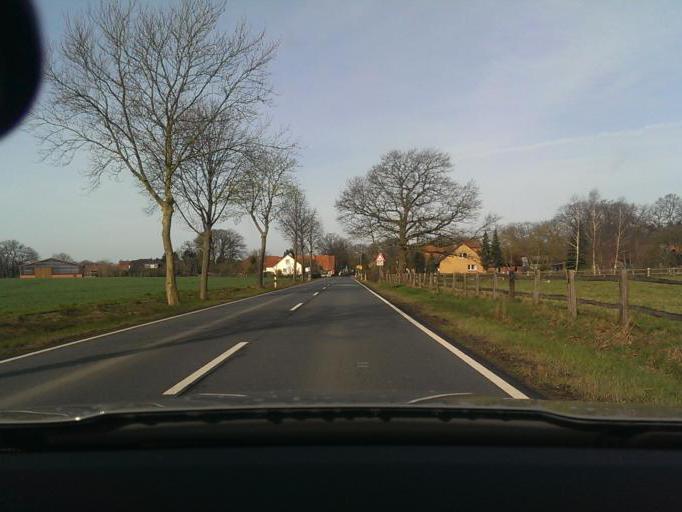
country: DE
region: Lower Saxony
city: Lindwedel
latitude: 52.5516
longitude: 9.6428
